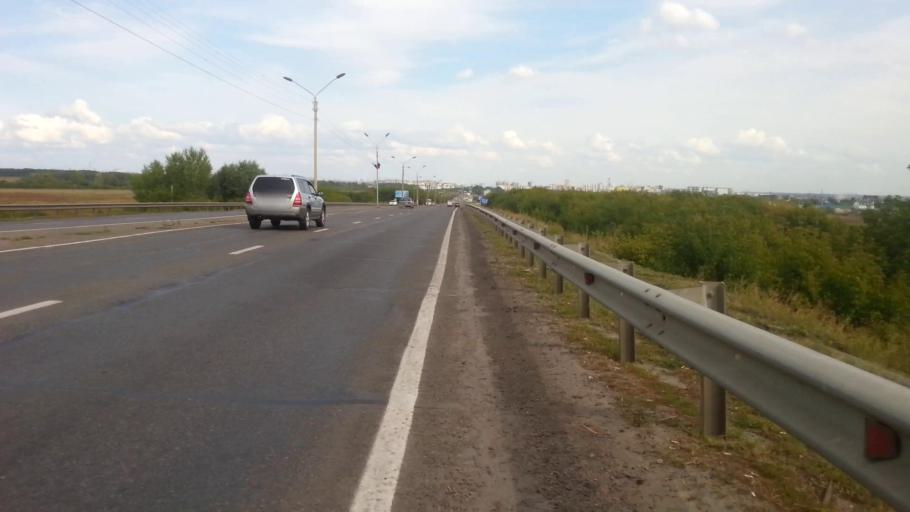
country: RU
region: Altai Krai
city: Novosilikatnyy
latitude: 53.3512
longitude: 83.5898
